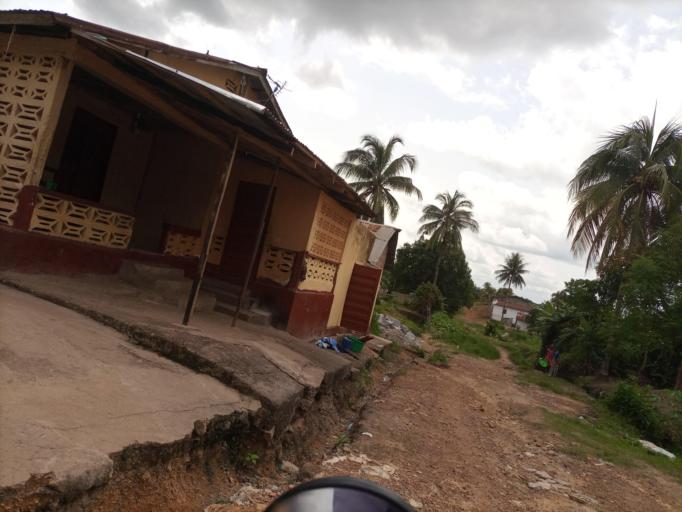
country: SL
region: Southern Province
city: Bo
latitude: 7.9519
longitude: -11.7367
